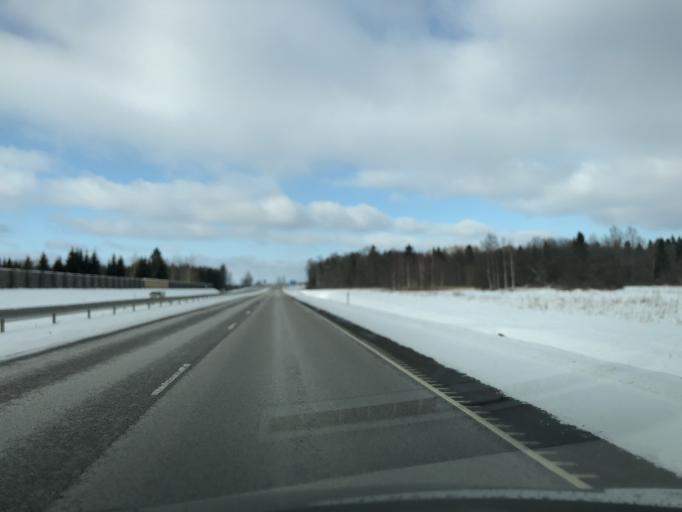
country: EE
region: Jaervamaa
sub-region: Paide linn
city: Paide
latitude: 58.9061
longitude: 25.6312
